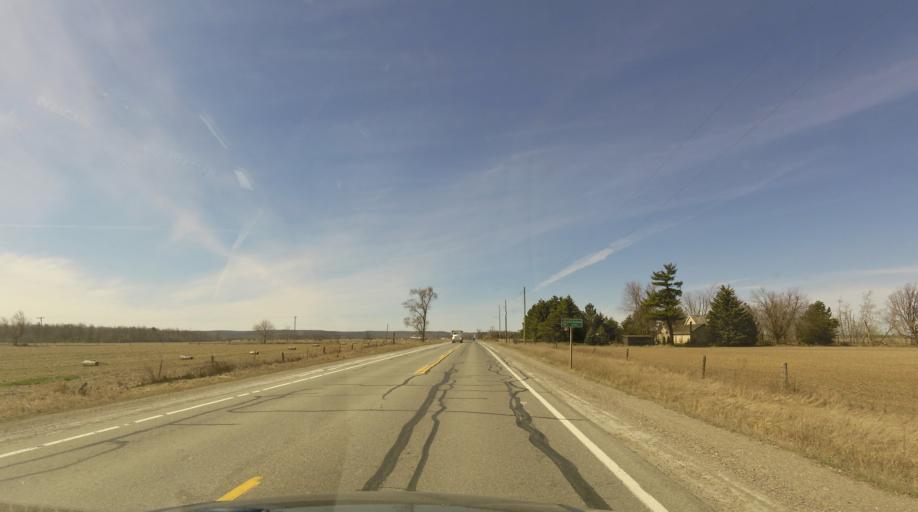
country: CA
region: Ontario
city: Brampton
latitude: 43.7133
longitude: -79.8924
